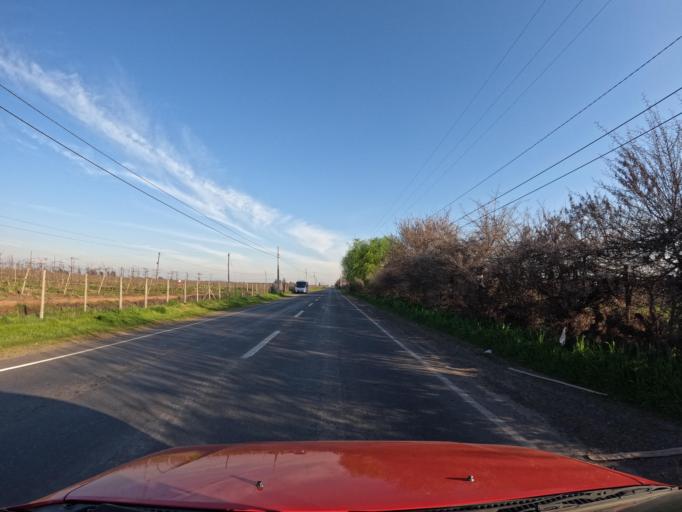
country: CL
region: Maule
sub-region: Provincia de Curico
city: Rauco
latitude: -34.9098
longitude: -71.2784
